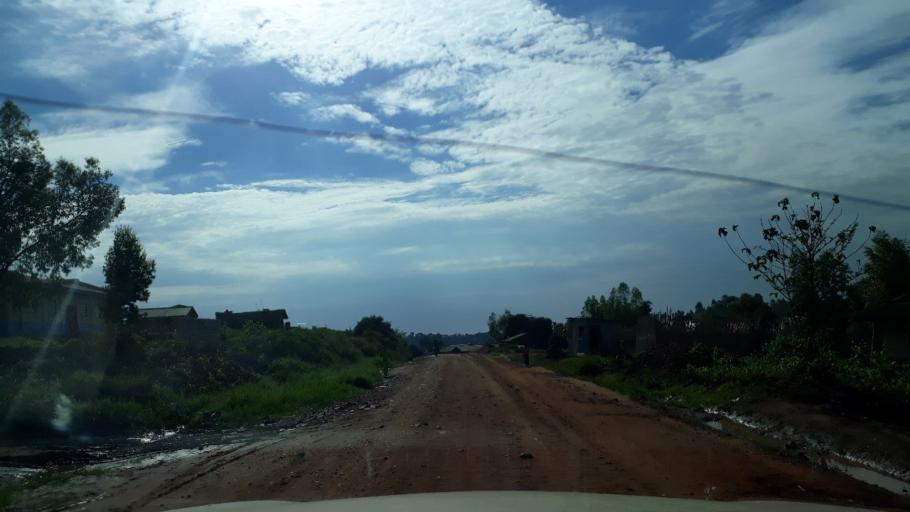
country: UG
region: Northern Region
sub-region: Zombo District
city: Paidha
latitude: 2.2988
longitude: 31.0004
